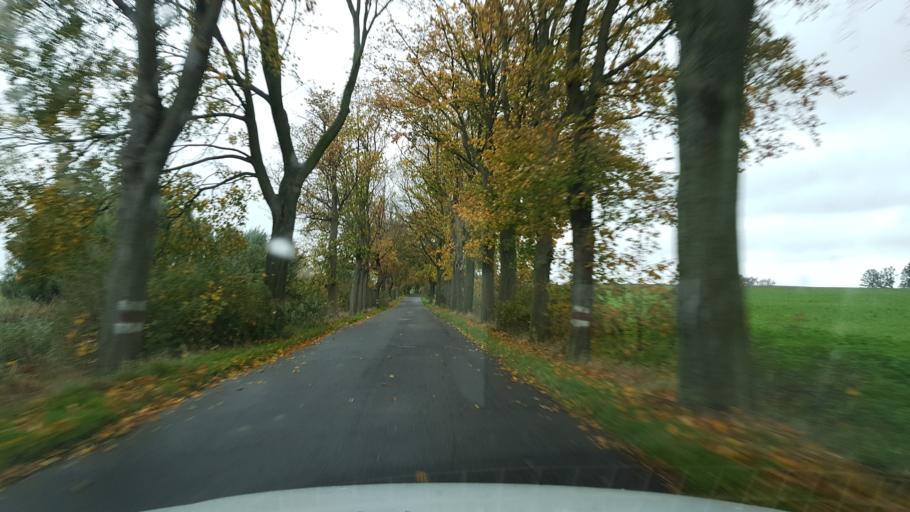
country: PL
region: West Pomeranian Voivodeship
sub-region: Powiat mysliborski
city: Mysliborz
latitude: 52.9765
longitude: 14.8798
